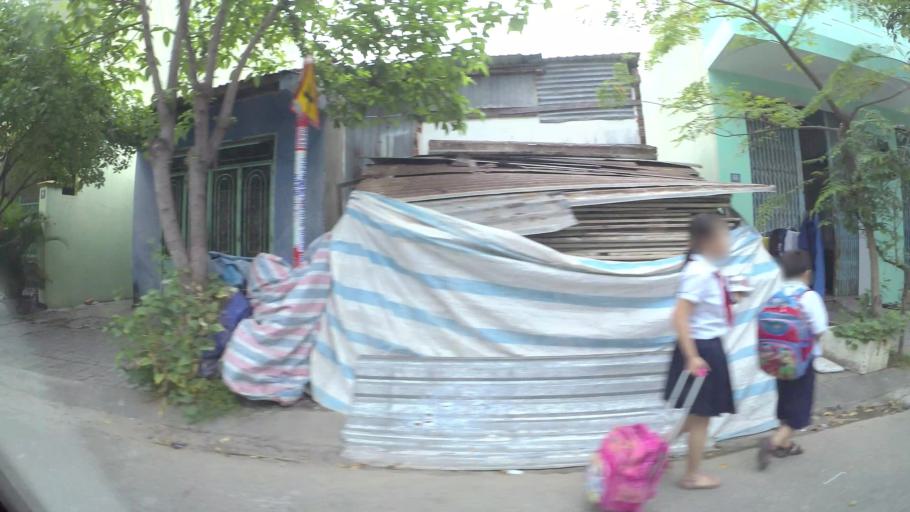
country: VN
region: Da Nang
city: Thanh Khe
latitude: 16.0599
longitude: 108.1818
